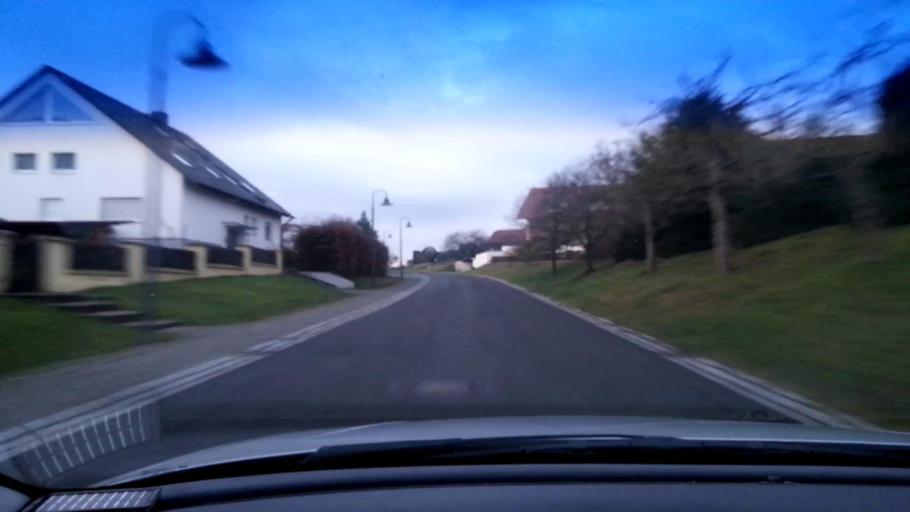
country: DE
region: Bavaria
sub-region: Upper Franconia
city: Frensdorf
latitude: 49.8250
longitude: 10.8867
